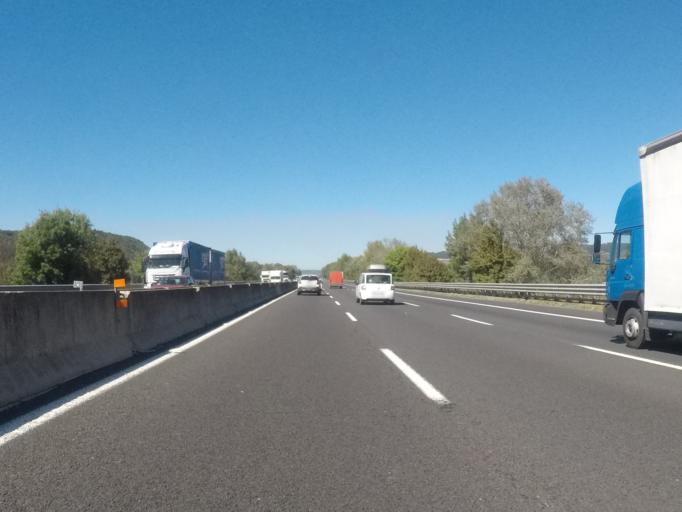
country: IT
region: Umbria
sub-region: Provincia di Terni
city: Otricoli
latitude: 42.4048
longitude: 12.4532
